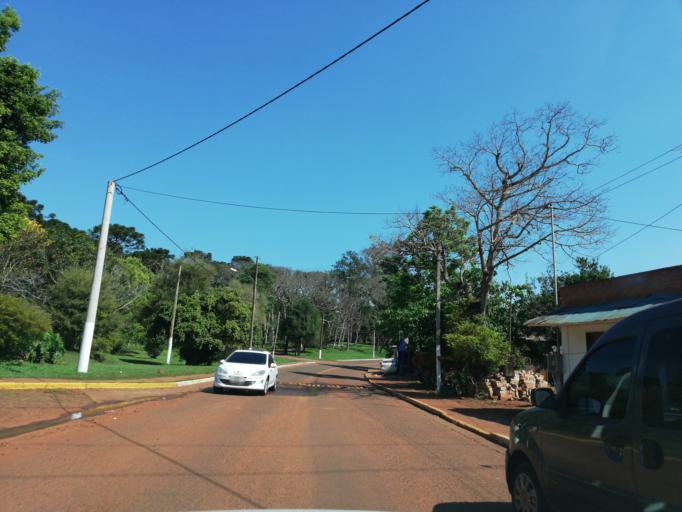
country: AR
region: Misiones
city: Puerto Eldorado
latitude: -26.4115
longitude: -54.6877
